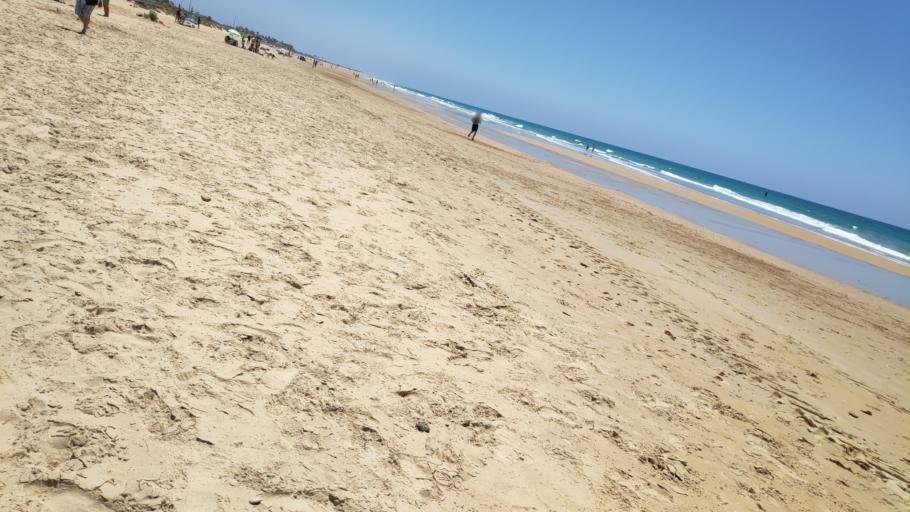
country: ES
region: Andalusia
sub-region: Provincia de Cadiz
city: Conil de la Frontera
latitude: 36.2313
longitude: -6.0709
